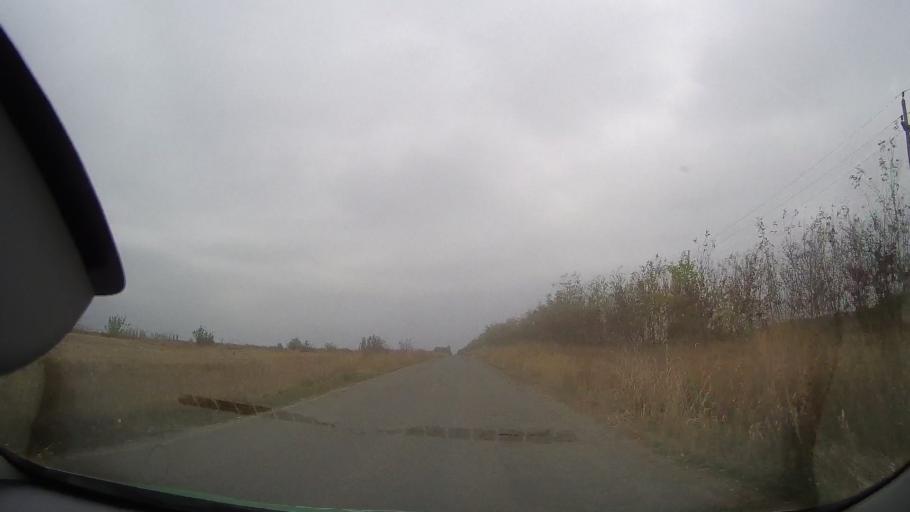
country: RO
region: Buzau
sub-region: Comuna Glodeanu-Silistea
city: Glodeanu-Silistea
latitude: 44.8146
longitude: 26.8473
